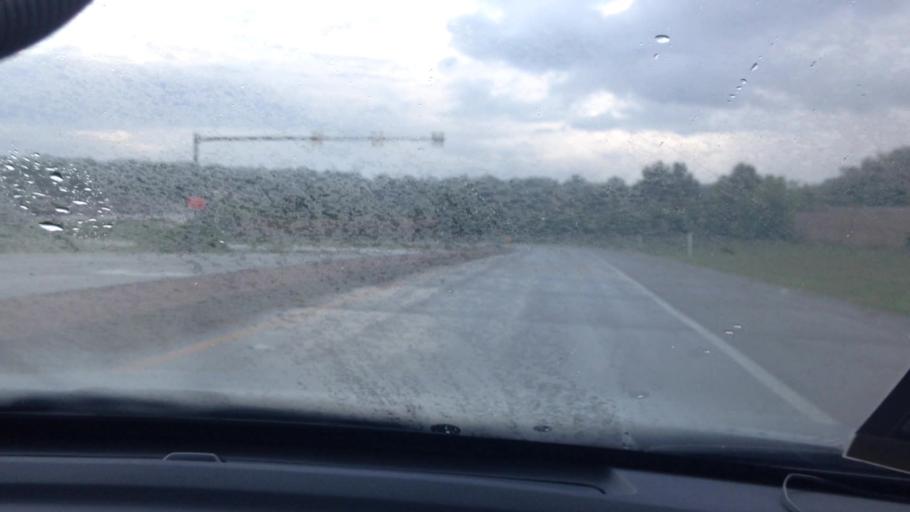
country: US
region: Kansas
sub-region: Johnson County
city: Lenexa
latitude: 38.9425
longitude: -94.7032
